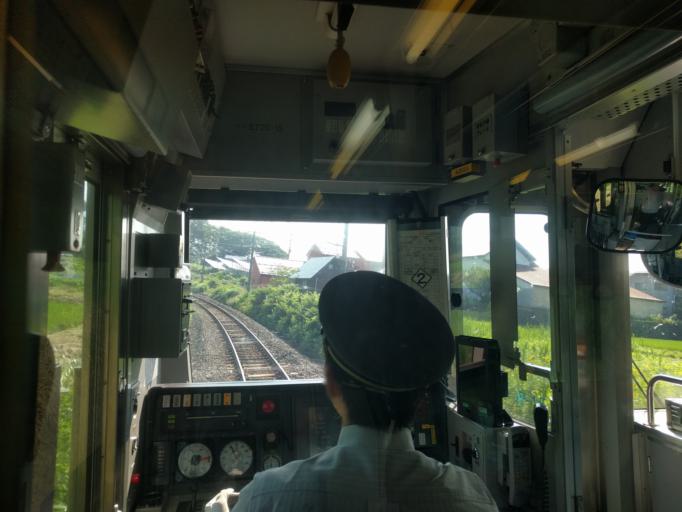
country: JP
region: Fukushima
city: Inawashiro
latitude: 37.5587
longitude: 139.9837
